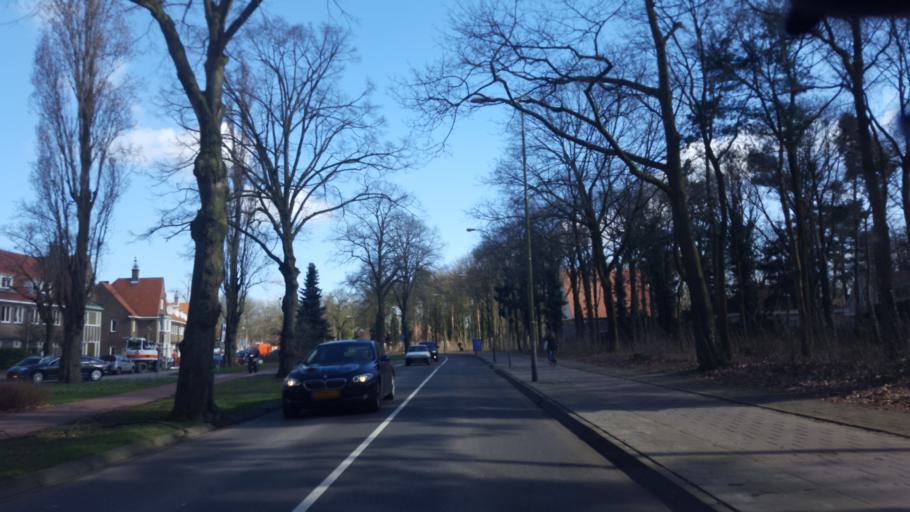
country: NL
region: North Brabant
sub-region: Gemeente Eindhoven
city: Lakerlopen
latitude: 51.4167
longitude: 5.5008
